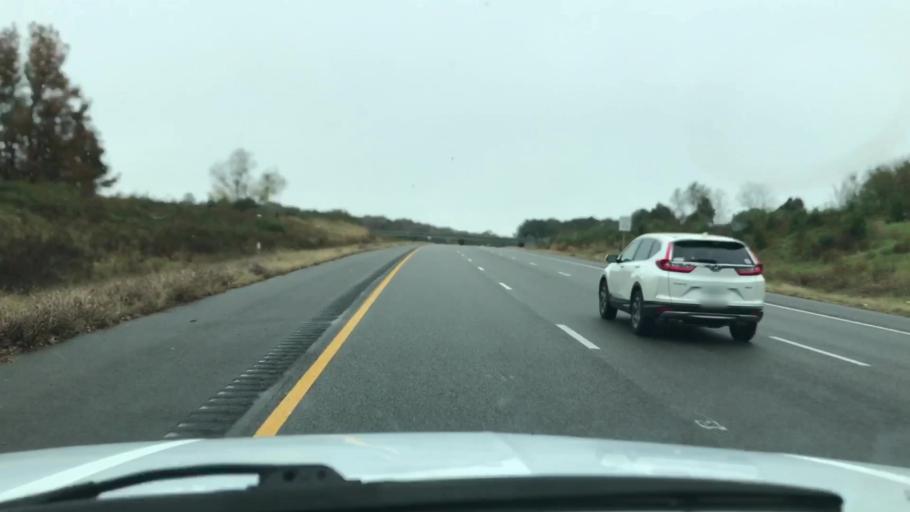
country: US
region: Virginia
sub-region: Henrico County
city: Glen Allen
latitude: 37.6817
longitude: -77.5272
